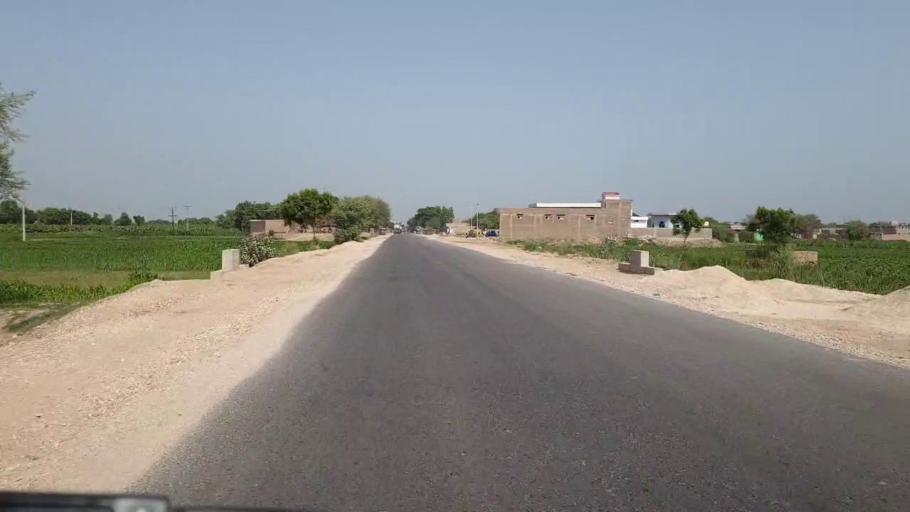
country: PK
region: Sindh
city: Sakrand
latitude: 26.2481
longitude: 68.2139
